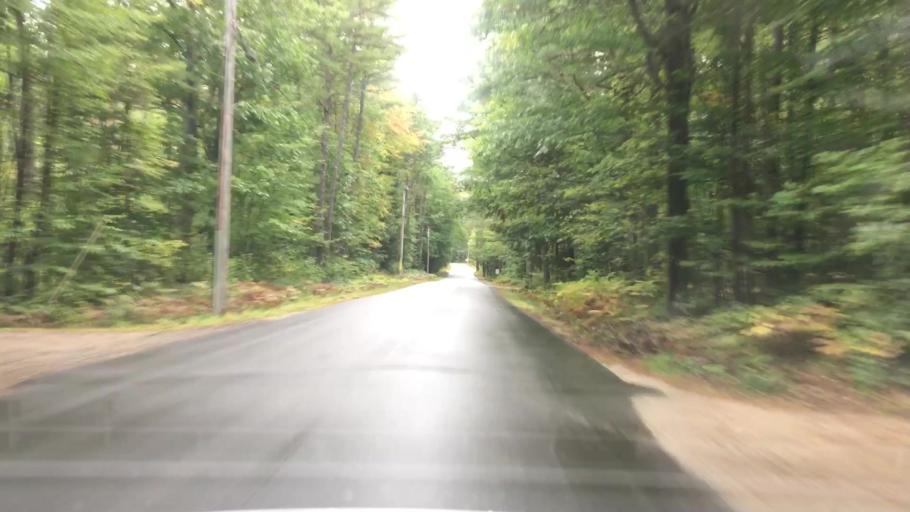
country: US
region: Maine
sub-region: Cumberland County
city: Raymond
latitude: 43.9930
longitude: -70.5662
